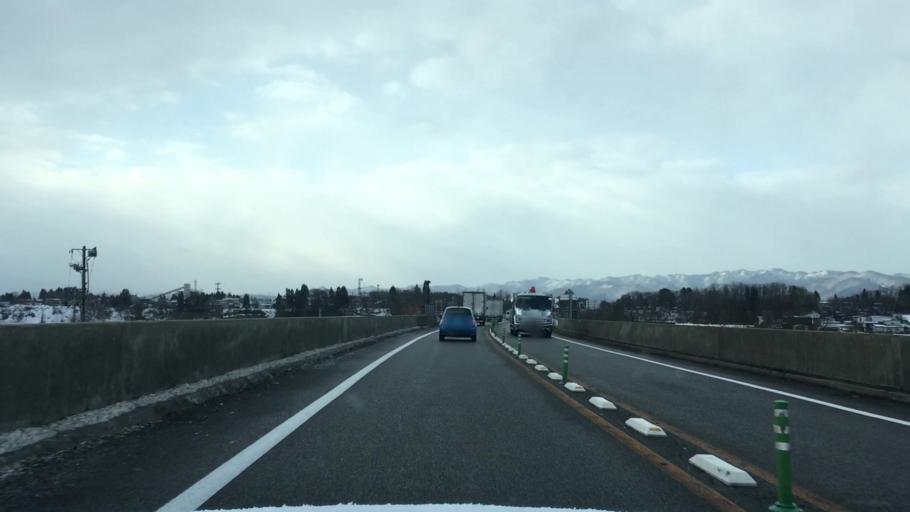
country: JP
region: Akita
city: Odate
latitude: 40.2827
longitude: 140.5401
